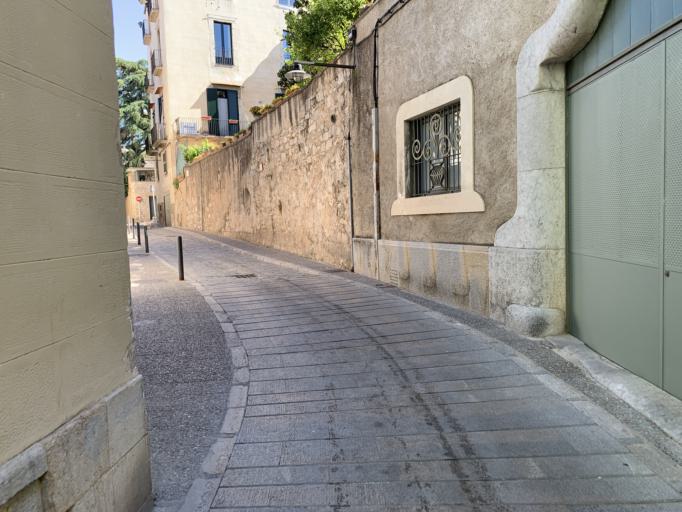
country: ES
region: Catalonia
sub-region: Provincia de Girona
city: Girona
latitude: 41.9834
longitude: 2.8268
